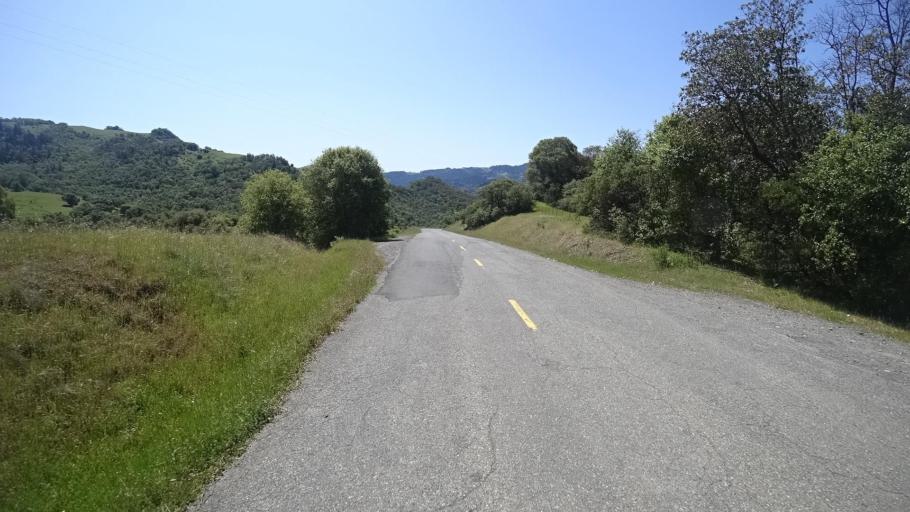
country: US
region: California
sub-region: Humboldt County
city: Redway
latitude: 40.1806
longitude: -123.5932
